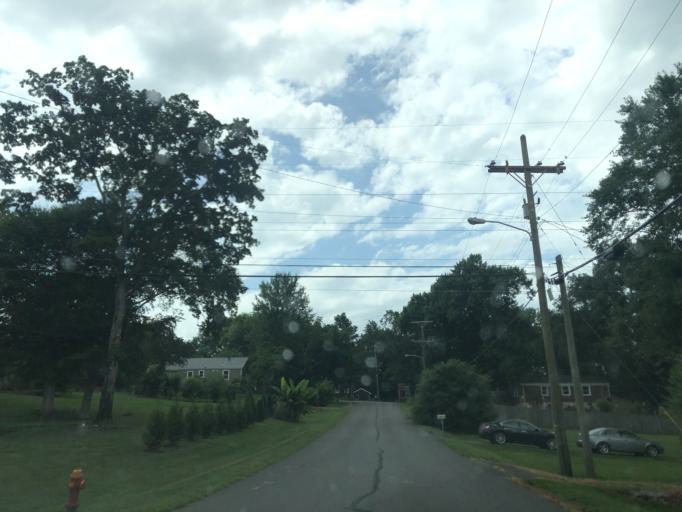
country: US
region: Tennessee
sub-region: Davidson County
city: Lakewood
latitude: 36.1619
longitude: -86.6559
